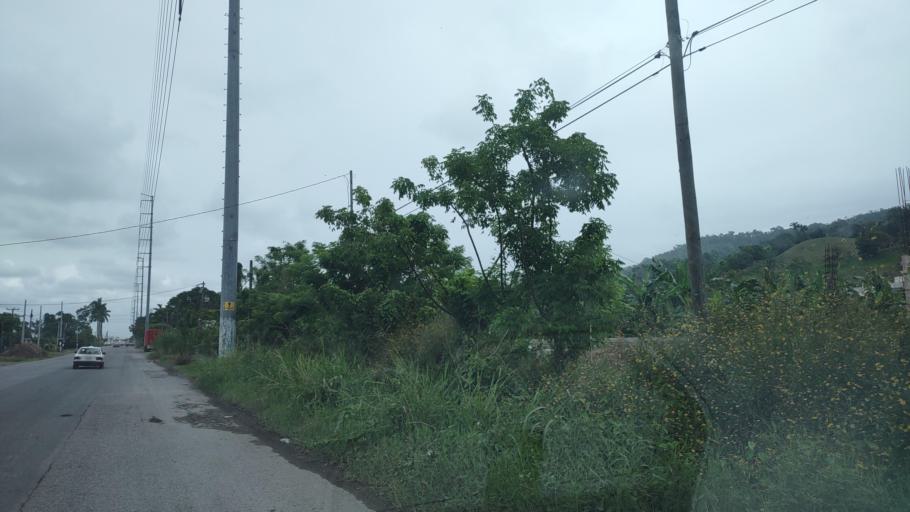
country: MX
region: Veracruz
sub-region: Papantla
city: Fraccionamiento la Florida
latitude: 20.5867
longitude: -97.4251
